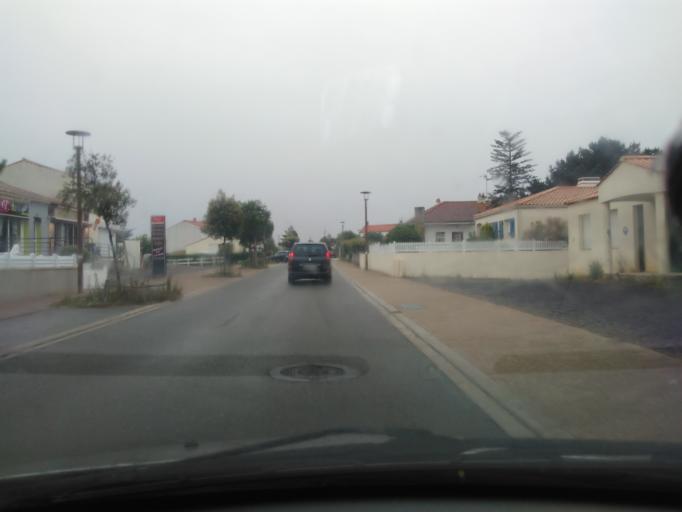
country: FR
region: Pays de la Loire
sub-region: Departement de la Vendee
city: Bretignolles-sur-Mer
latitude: 46.6299
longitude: -1.8590
